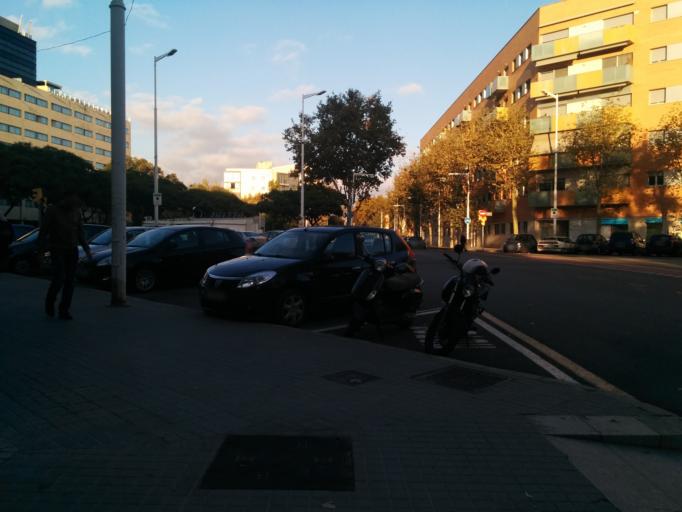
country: ES
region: Catalonia
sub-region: Provincia de Barcelona
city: Ciutat Vella
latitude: 41.3921
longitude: 2.1924
